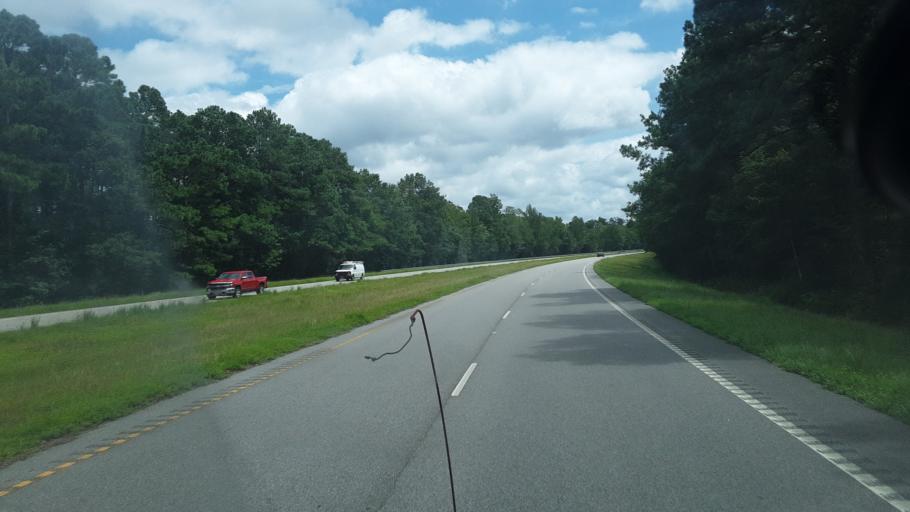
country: US
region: North Carolina
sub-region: Columbus County
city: Tabor City
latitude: 34.1185
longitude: -78.9707
